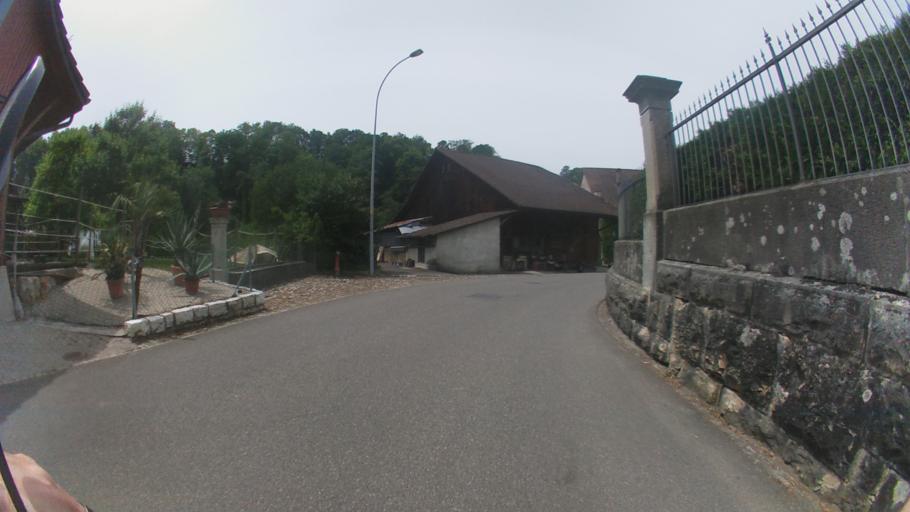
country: CH
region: Aargau
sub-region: Bezirk Zurzach
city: Tegerfelden
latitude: 47.5567
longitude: 8.2896
